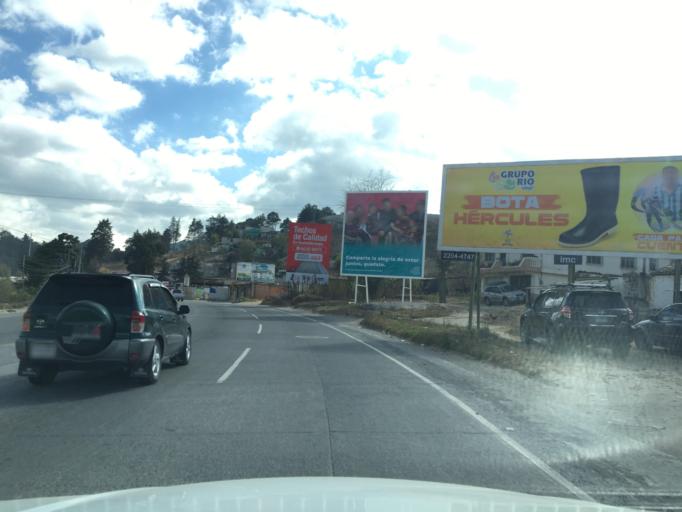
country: GT
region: Quetzaltenango
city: Salcaja
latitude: 14.8541
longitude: -91.4769
